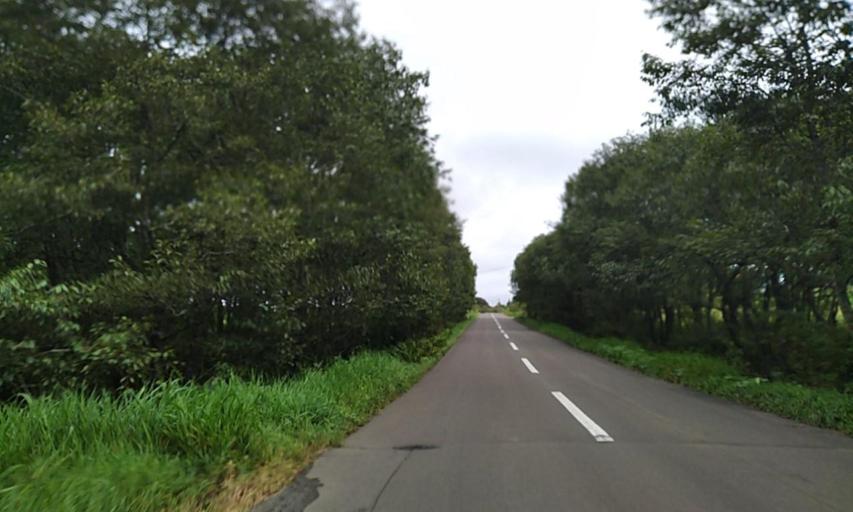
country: JP
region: Hokkaido
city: Nemuro
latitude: 43.2720
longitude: 145.2765
